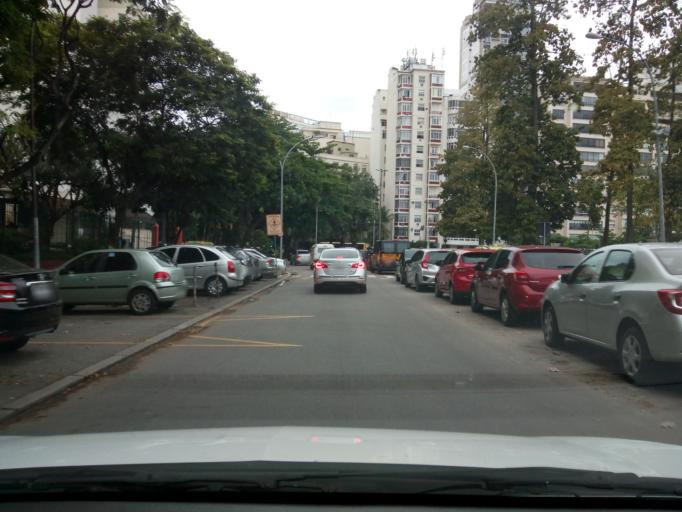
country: BR
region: Rio de Janeiro
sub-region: Rio De Janeiro
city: Rio de Janeiro
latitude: -22.9384
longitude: -43.1724
